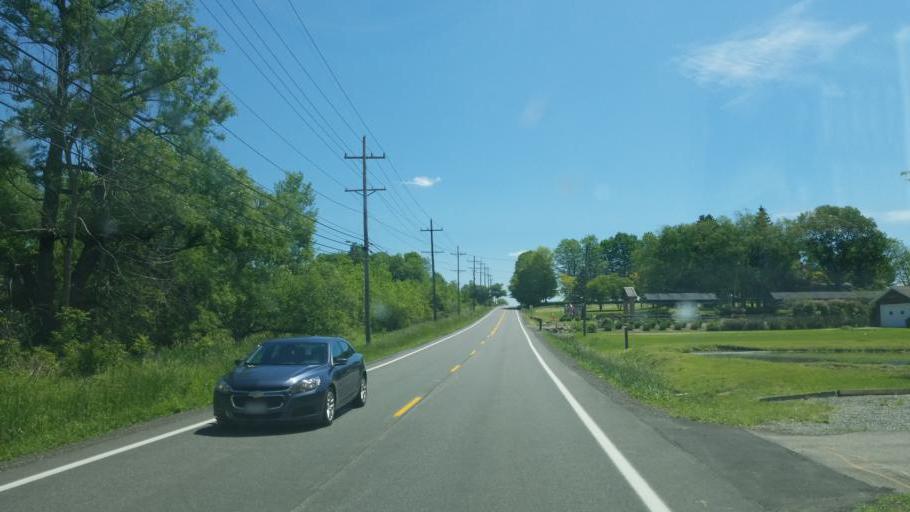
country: US
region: Ohio
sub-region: Geauga County
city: Burton
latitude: 41.4636
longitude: -81.1173
